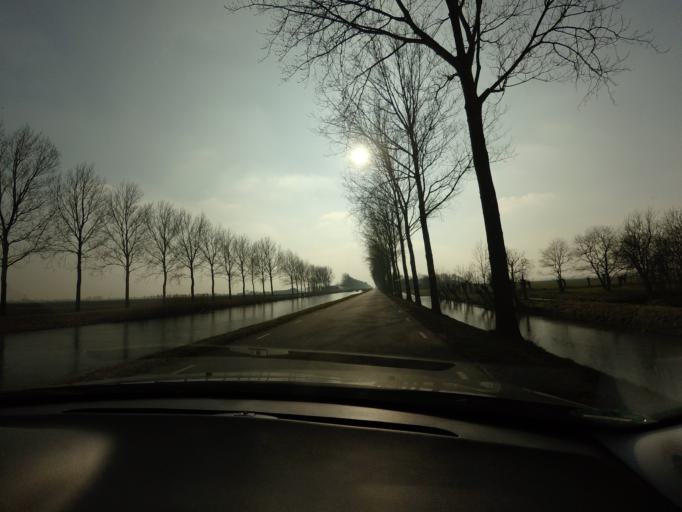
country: NL
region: North Holland
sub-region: Gemeente Alkmaar
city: Alkmaar
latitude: 52.6032
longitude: 4.7896
